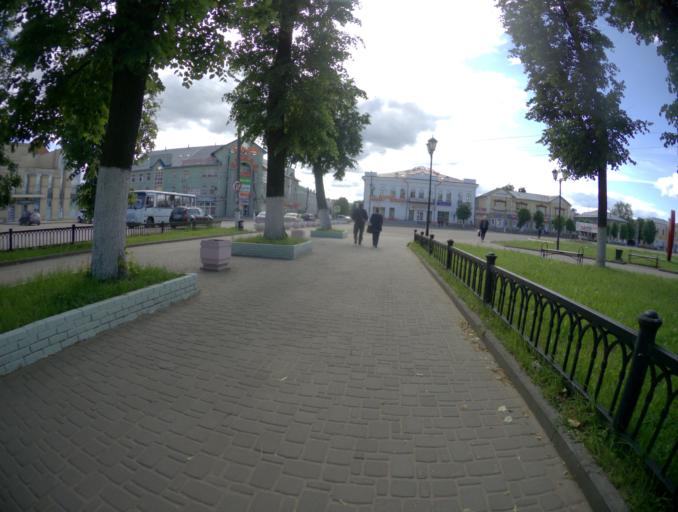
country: RU
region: Ivanovo
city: Shuya
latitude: 56.8541
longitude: 41.3816
